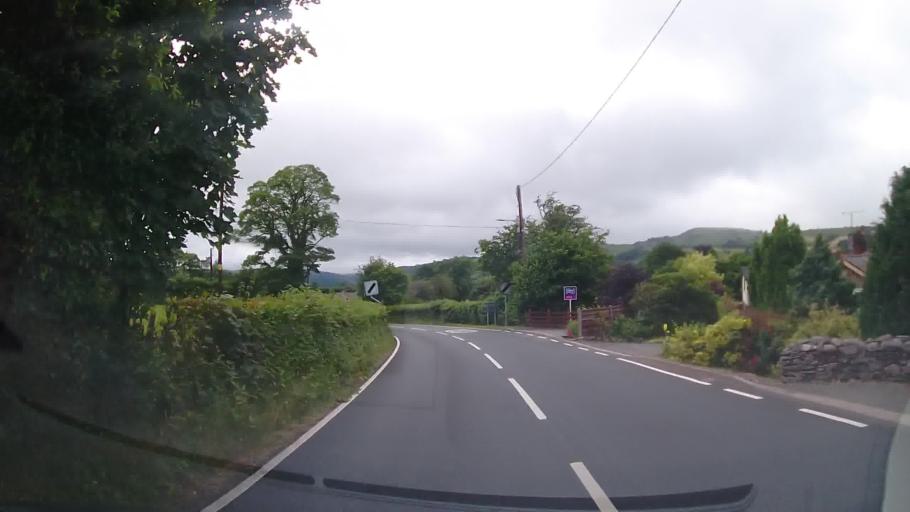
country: GB
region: Wales
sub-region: Denbighshire
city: Corwen
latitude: 52.9561
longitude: -3.4079
